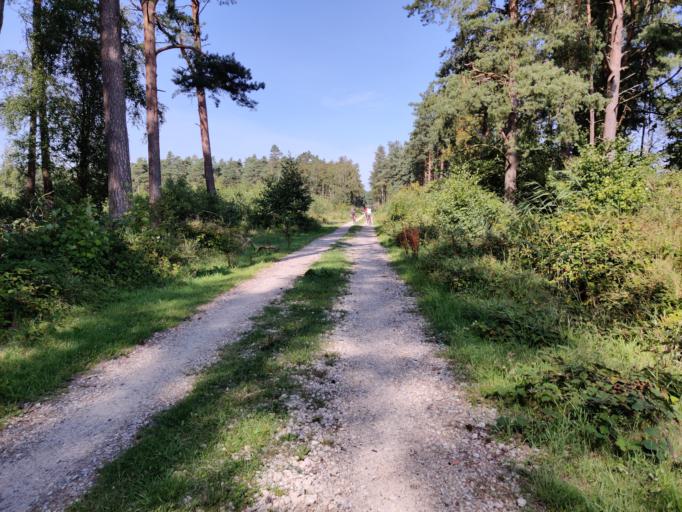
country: DK
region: Zealand
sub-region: Guldborgsund Kommune
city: Nykobing Falster
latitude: 54.6280
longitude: 11.9582
